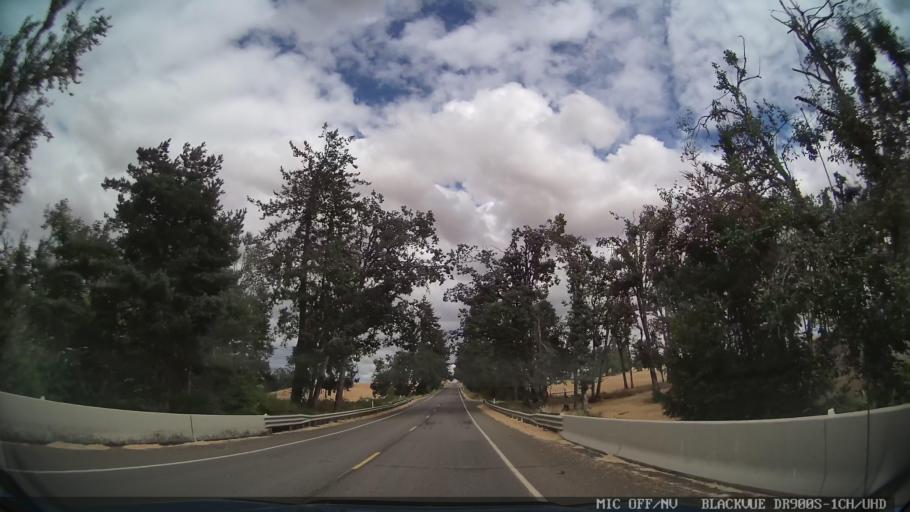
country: US
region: Oregon
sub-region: Marion County
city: Sublimity
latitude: 44.8655
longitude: -122.8244
